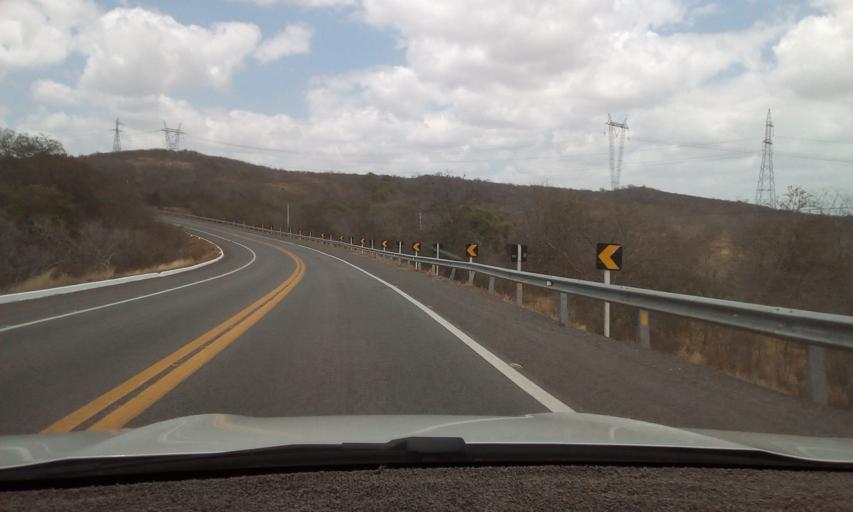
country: BR
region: Paraiba
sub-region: Boqueirao
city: Boqueirao
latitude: -7.6178
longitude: -36.0754
